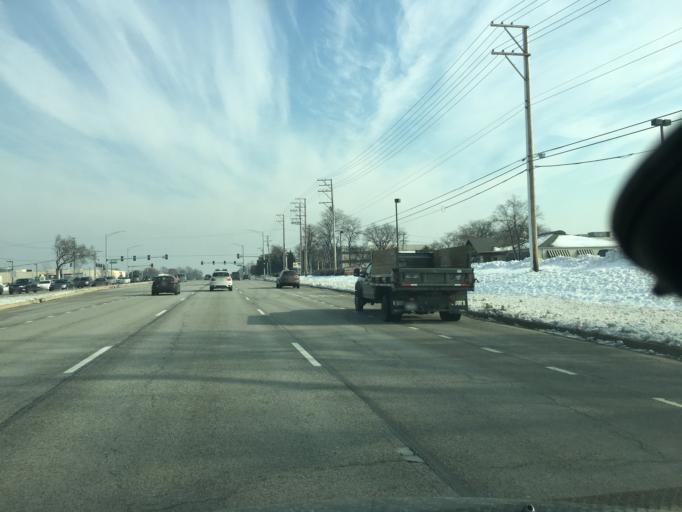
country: US
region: Illinois
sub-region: DuPage County
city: Woodridge
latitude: 41.7509
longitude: -88.0152
